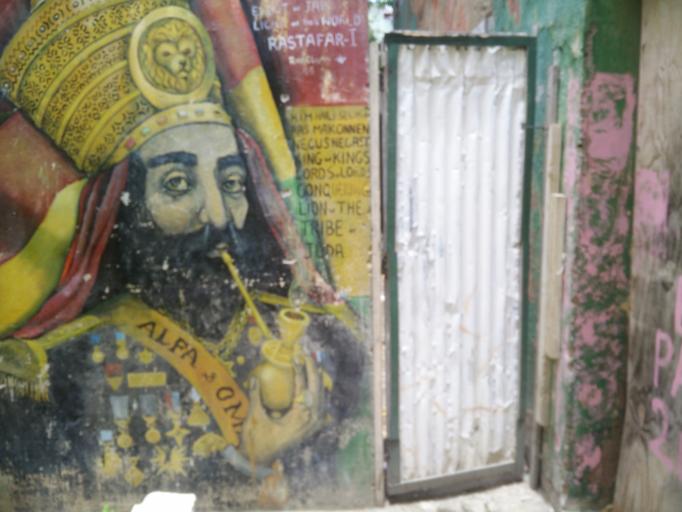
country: CW
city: Willemstad
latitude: 12.1098
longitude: -68.9388
